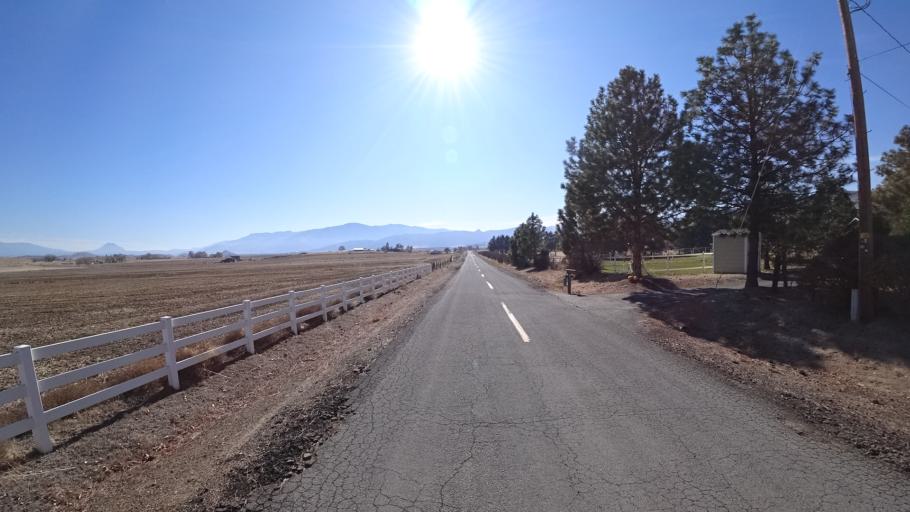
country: US
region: California
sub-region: Siskiyou County
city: Montague
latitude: 41.5842
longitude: -122.5445
